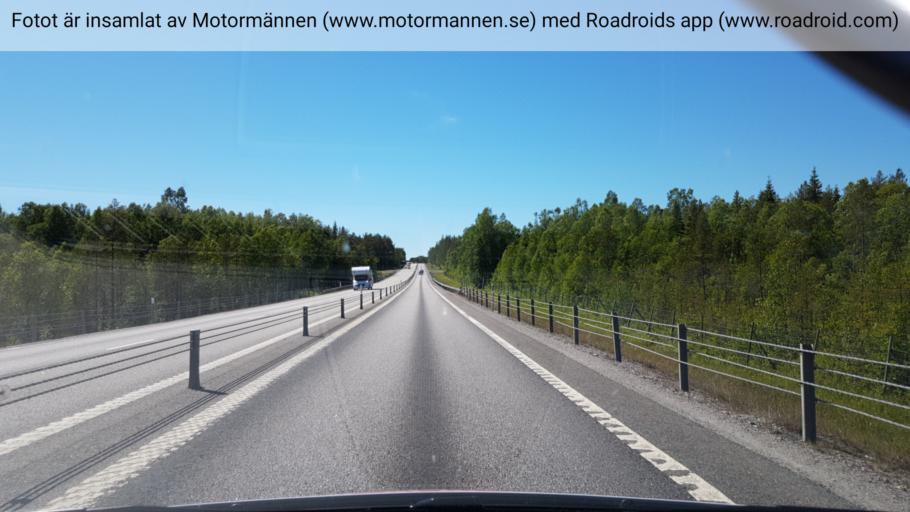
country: SE
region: Norrbotten
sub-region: Pitea Kommun
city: Hortlax
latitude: 65.0582
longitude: 21.4101
